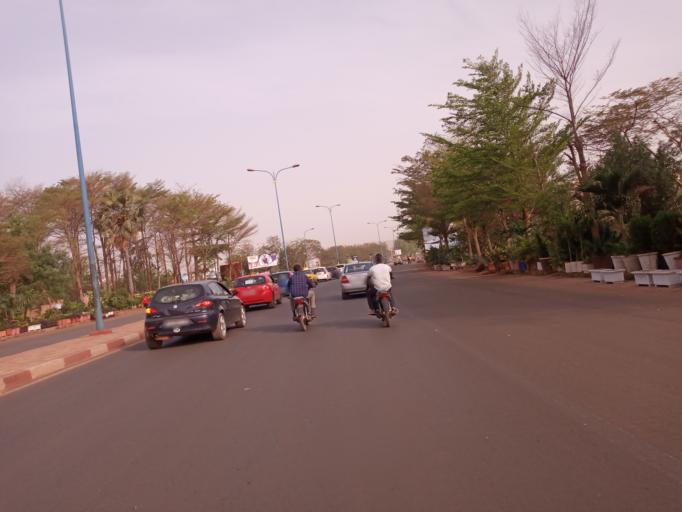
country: ML
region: Bamako
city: Bamako
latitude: 12.6397
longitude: -8.0200
